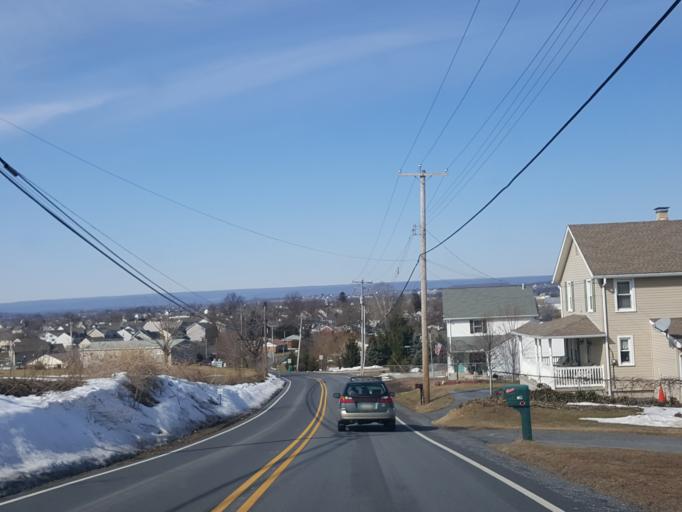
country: US
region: Pennsylvania
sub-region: Lebanon County
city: Campbelltown
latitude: 40.2721
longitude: -76.5669
